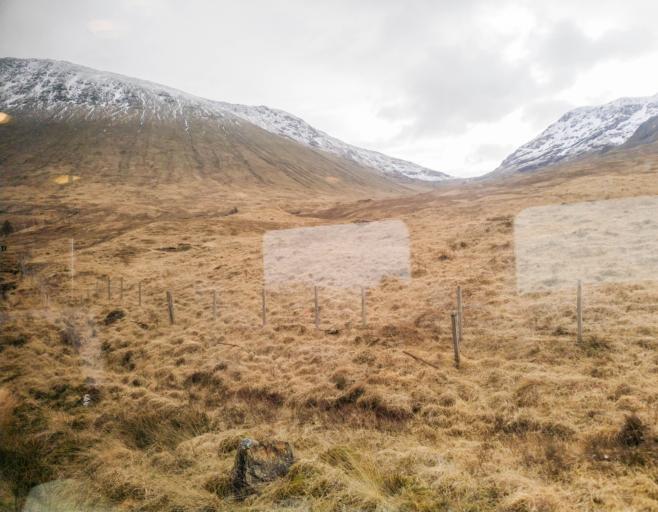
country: GB
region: Scotland
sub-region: Highland
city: Spean Bridge
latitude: 56.5554
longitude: -4.7328
